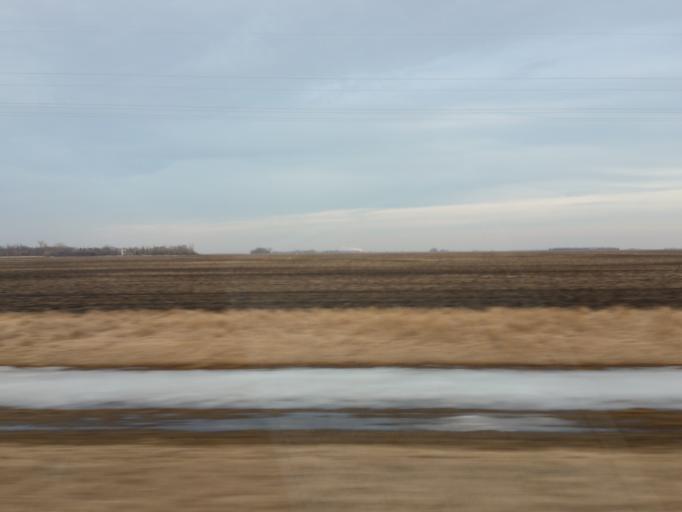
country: US
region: North Dakota
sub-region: Traill County
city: Mayville
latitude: 47.4361
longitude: -97.3259
